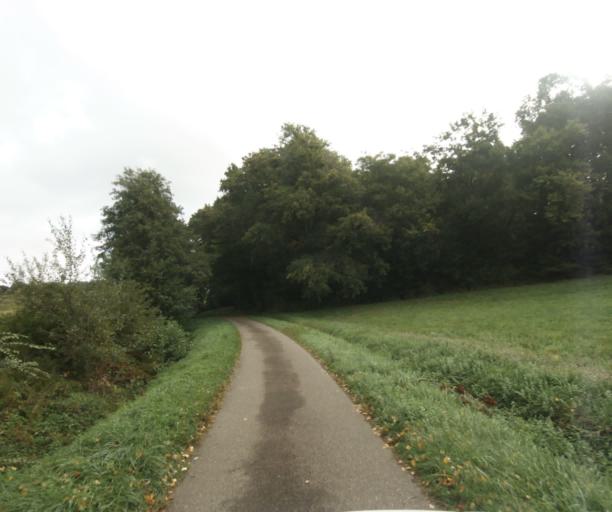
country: FR
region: Midi-Pyrenees
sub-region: Departement du Gers
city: Nogaro
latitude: 43.8272
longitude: -0.0786
